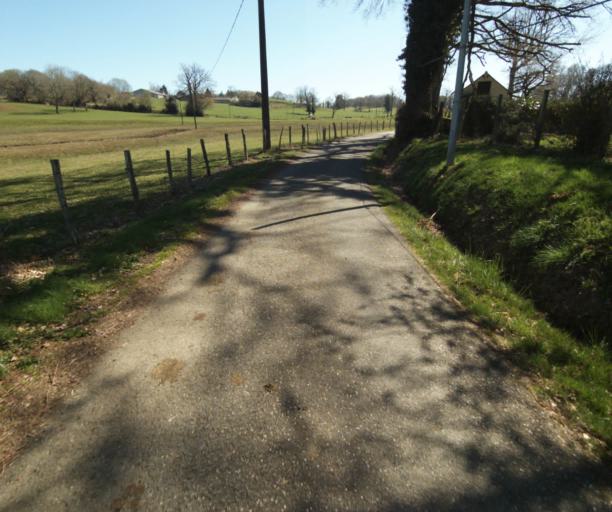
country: FR
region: Limousin
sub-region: Departement de la Correze
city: Uzerche
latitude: 45.4005
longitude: 1.6304
